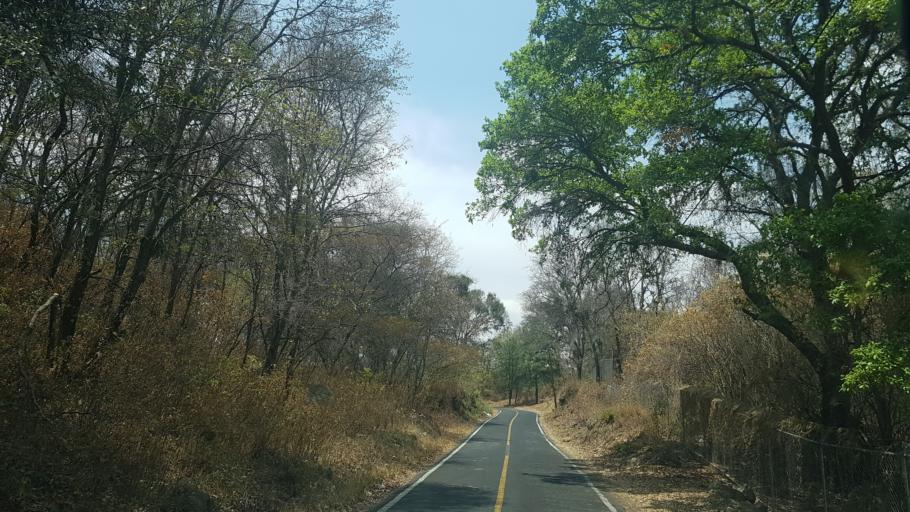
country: MX
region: Puebla
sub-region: Tochimilco
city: La Magdalena Yancuitlalpan
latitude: 18.8850
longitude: -98.5892
